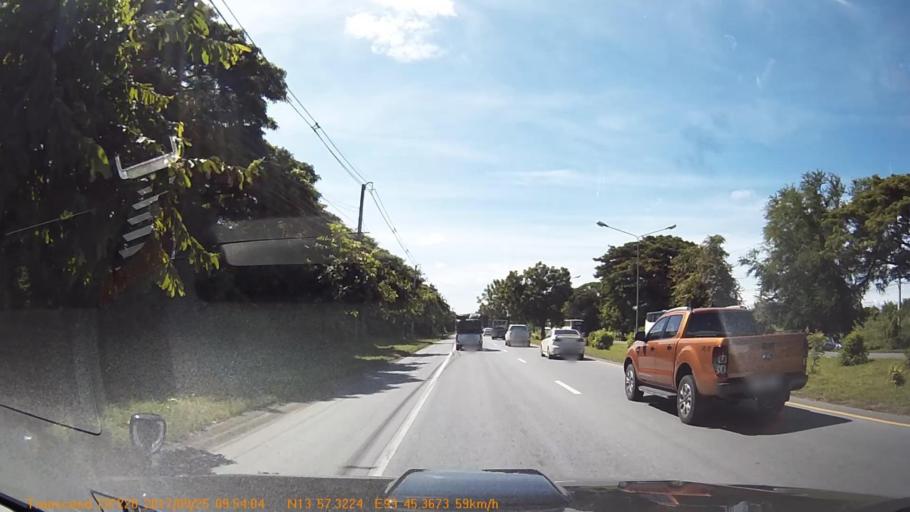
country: TH
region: Kanchanaburi
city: Tha Maka
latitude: 13.9551
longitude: 99.7562
